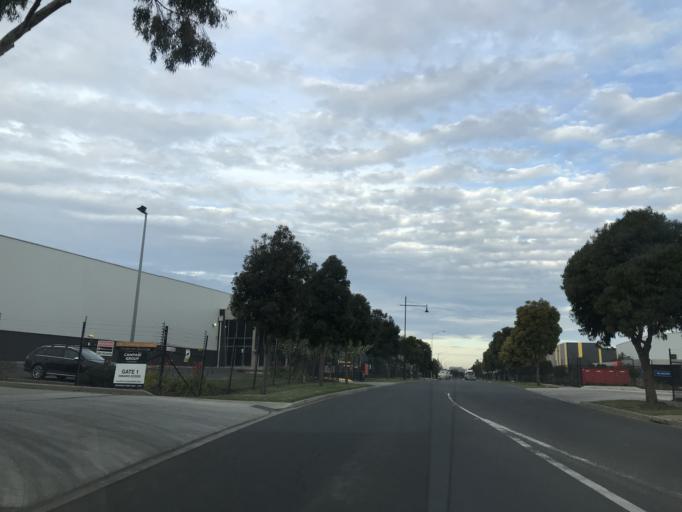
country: AU
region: Victoria
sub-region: Brimbank
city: Derrimut
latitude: -37.7996
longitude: 144.7594
